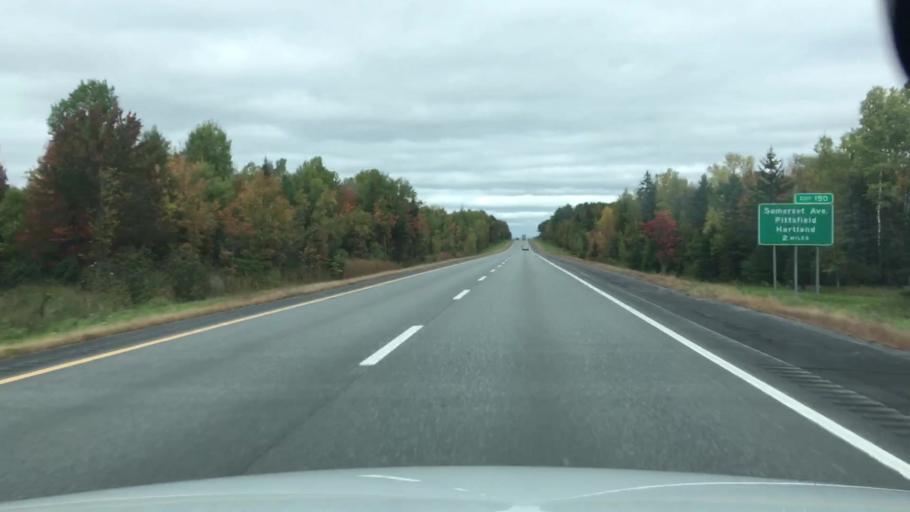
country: US
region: Maine
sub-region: Somerset County
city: Pittsfield
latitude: 44.7543
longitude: -69.4196
